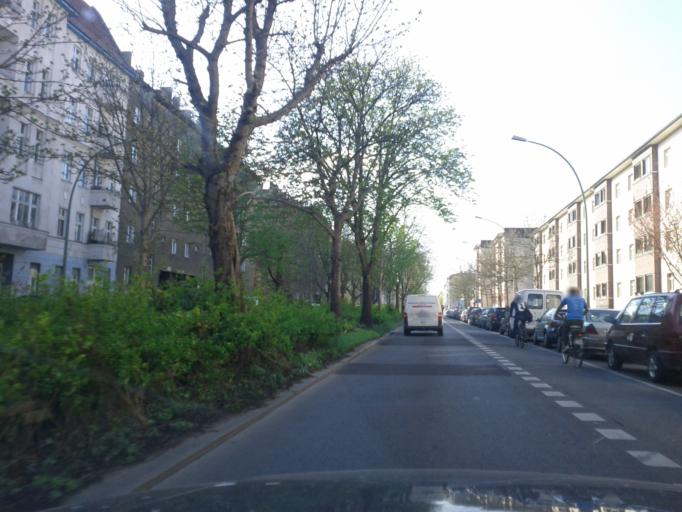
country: DE
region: Berlin
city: Prenzlauer Berg Bezirk
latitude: 52.5440
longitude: 13.4319
